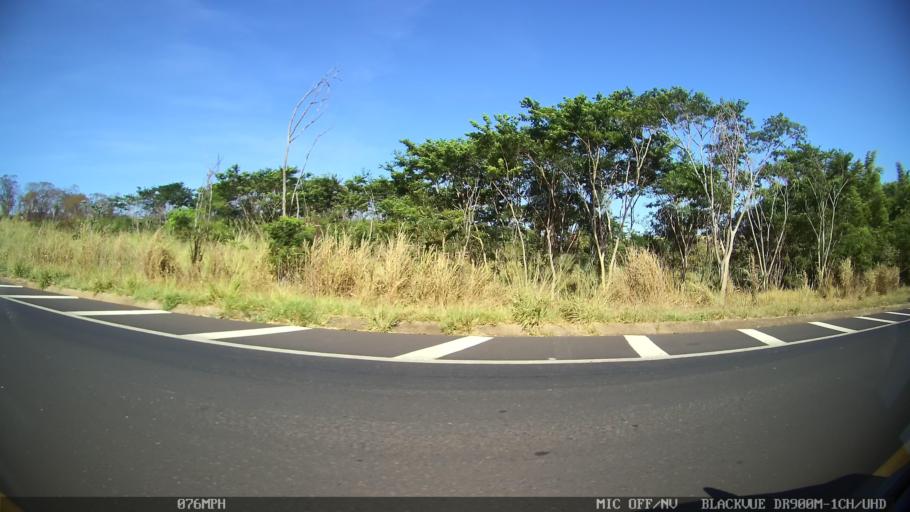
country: BR
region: Sao Paulo
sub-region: Barretos
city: Barretos
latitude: -20.6143
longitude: -48.7576
